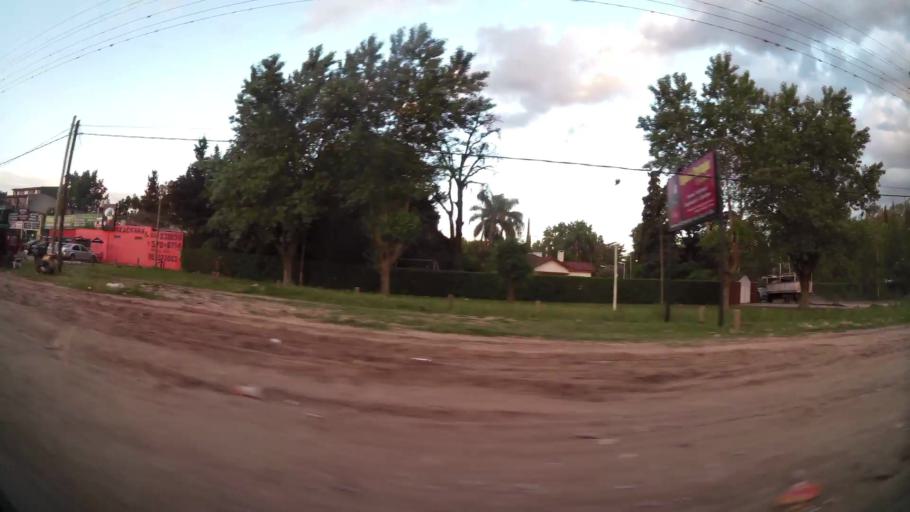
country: AR
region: Buenos Aires
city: Santa Catalina - Dique Lujan
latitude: -34.4864
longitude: -58.7740
